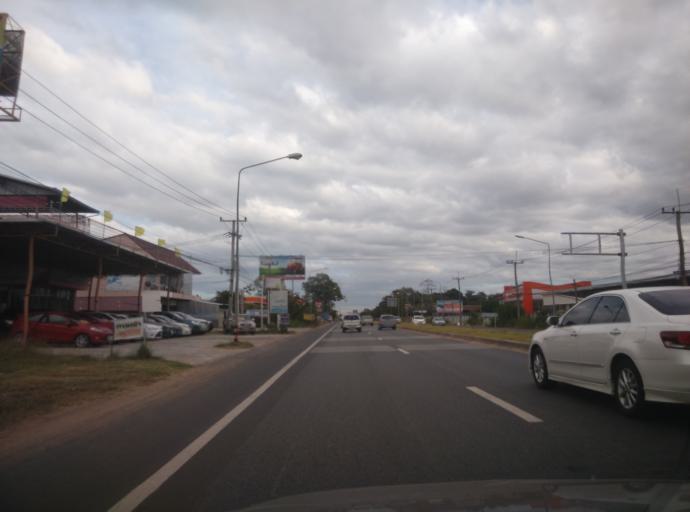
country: TH
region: Sisaket
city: Si Sa Ket
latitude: 15.1259
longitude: 104.2874
